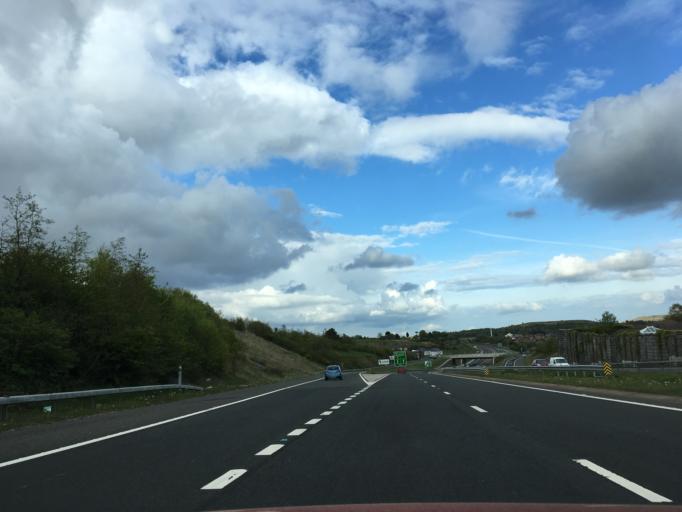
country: GB
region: Wales
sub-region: Blaenau Gwent
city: Tredegar
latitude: 51.7872
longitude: -3.2667
